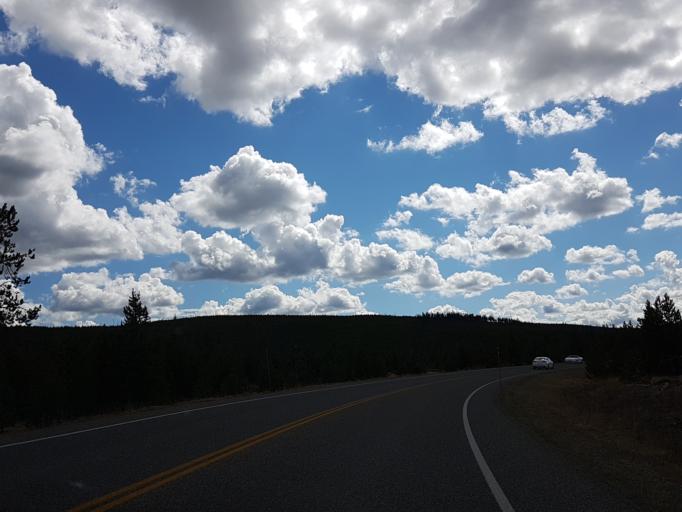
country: US
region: Montana
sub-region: Gallatin County
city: West Yellowstone
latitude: 44.5194
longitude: -110.8250
